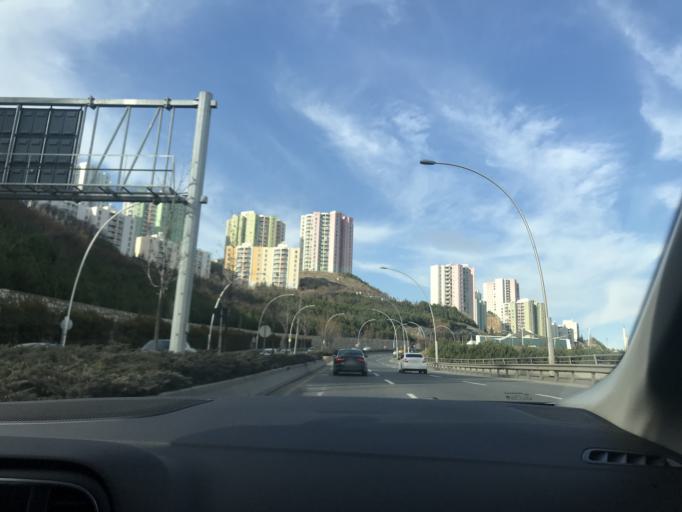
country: TR
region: Ankara
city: Mamak
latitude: 39.9962
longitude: 32.8967
